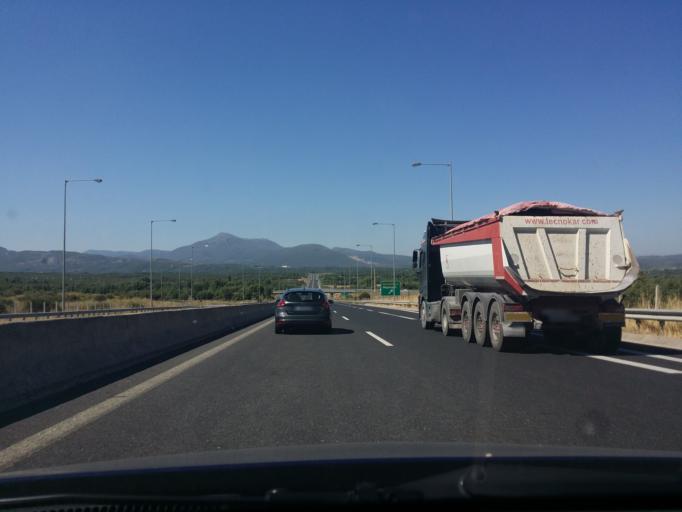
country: GR
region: Peloponnese
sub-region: Nomos Arkadias
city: Megalopoli
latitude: 37.3850
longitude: 22.1675
